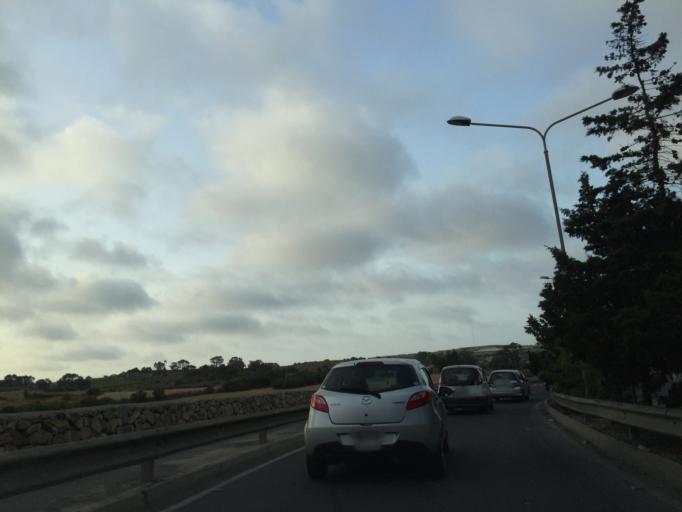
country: MT
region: L-Imtarfa
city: Imtarfa
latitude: 35.9018
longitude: 14.4081
